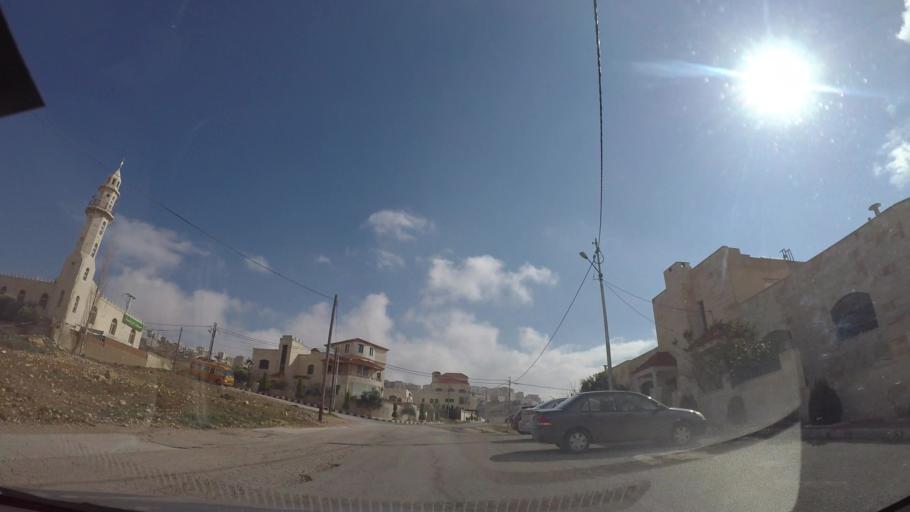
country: JO
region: Amman
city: Al Jubayhah
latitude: 32.0714
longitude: 35.8706
